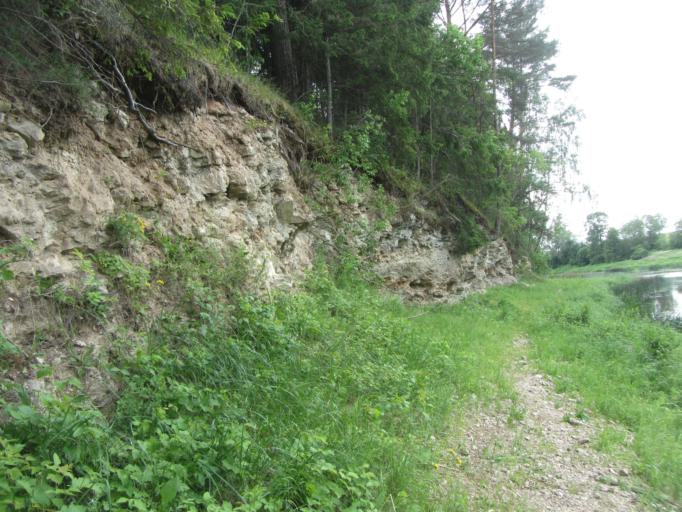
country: LT
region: Panevezys
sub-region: Birzai
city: Birzai
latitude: 56.4113
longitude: 24.8035
